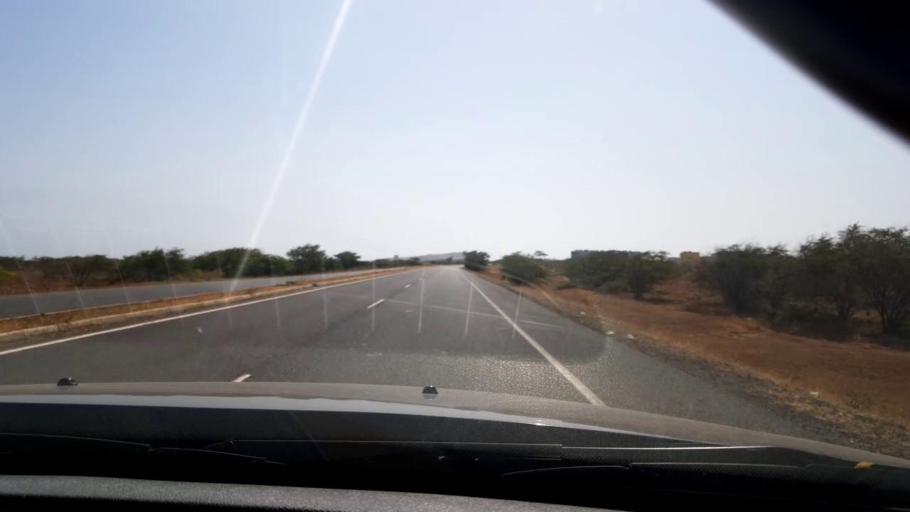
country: CV
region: Praia
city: Praia
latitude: 14.9567
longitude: -23.4951
